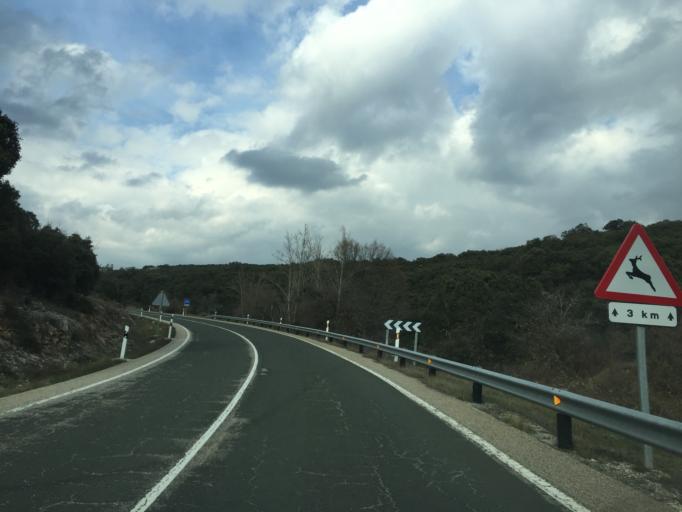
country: ES
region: Cantabria
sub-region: Provincia de Cantabria
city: San Martin de Elines
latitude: 42.8188
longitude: -3.7685
